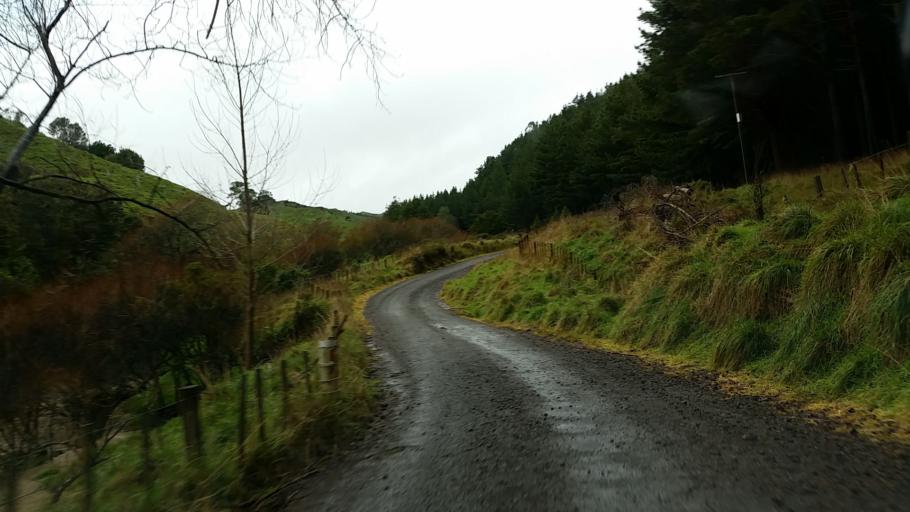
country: NZ
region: Taranaki
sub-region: South Taranaki District
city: Eltham
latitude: -39.5030
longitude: 174.4079
